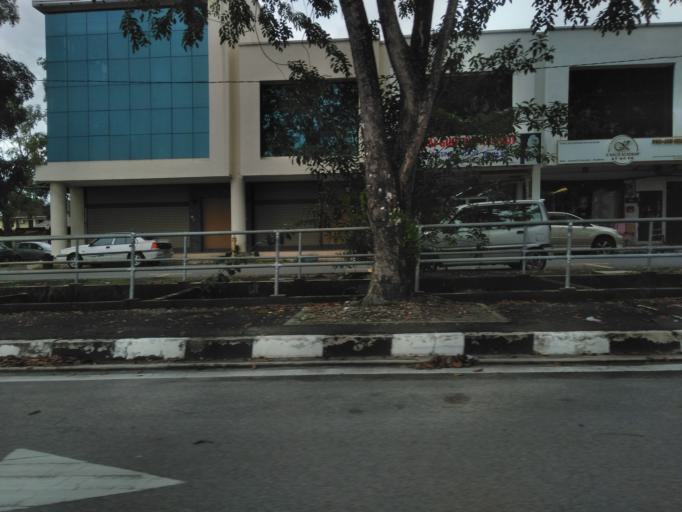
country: MY
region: Penang
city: Bukit Mertajam
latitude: 5.3323
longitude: 100.4846
